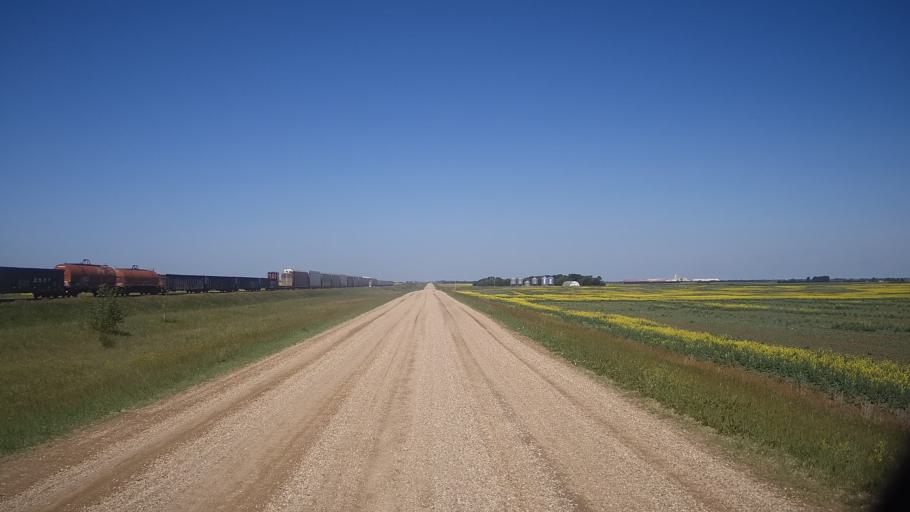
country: CA
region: Saskatchewan
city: Watrous
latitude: 51.8601
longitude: -105.9620
